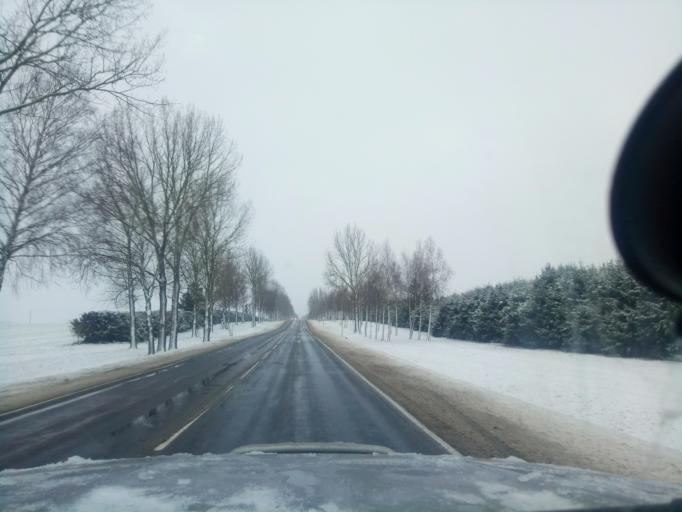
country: BY
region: Minsk
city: Haradzyeya
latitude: 53.3517
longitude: 26.5169
